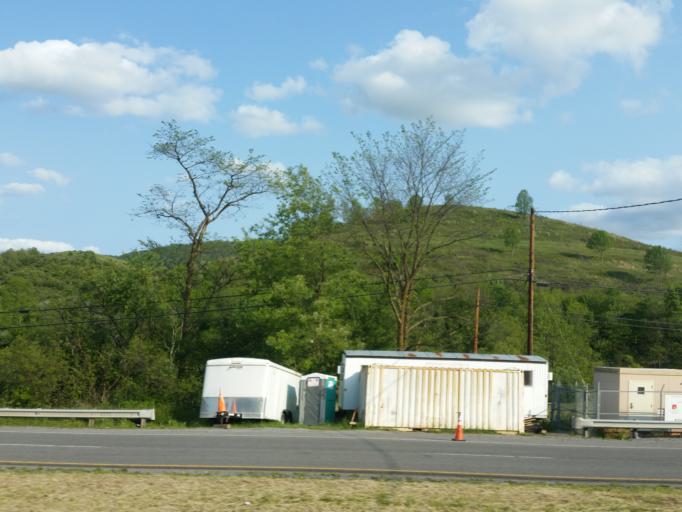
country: US
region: Virginia
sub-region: Tazewell County
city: Tazewell
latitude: 37.1559
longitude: -81.4758
